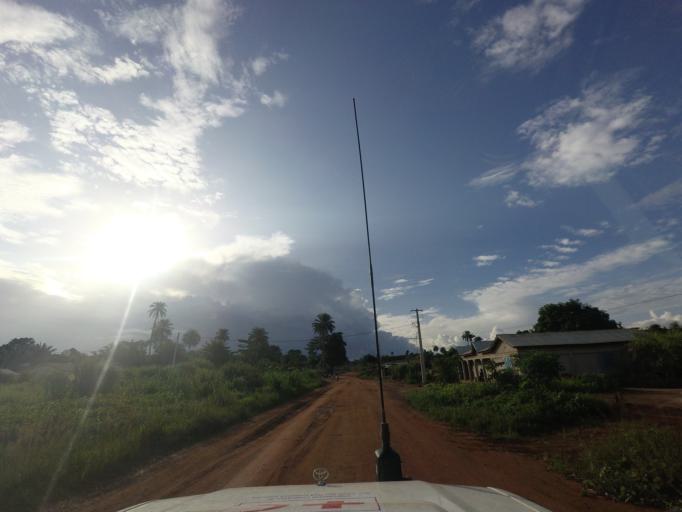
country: GN
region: Nzerekore
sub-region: Nzerekore Prefecture
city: Nzerekore
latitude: 7.7192
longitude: -8.8228
